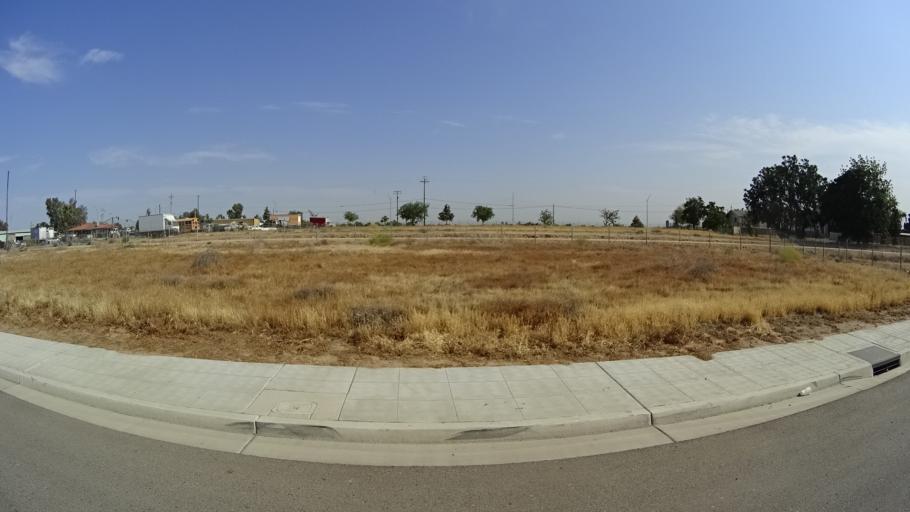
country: US
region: California
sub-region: Fresno County
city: West Park
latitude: 36.7419
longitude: -119.8426
